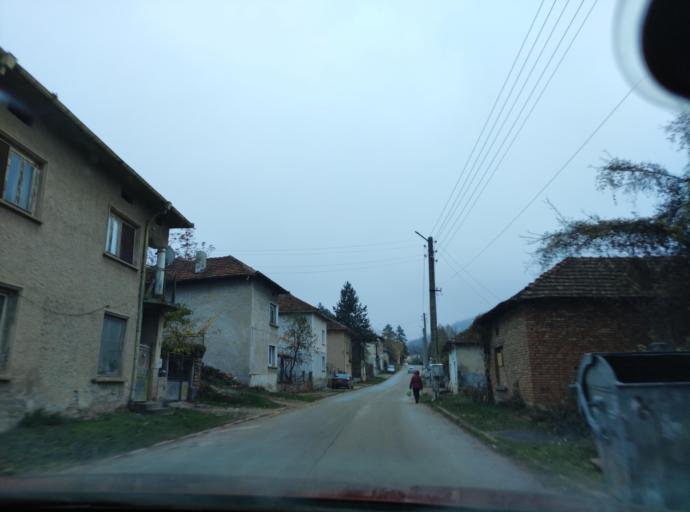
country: BG
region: Lovech
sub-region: Obshtina Yablanitsa
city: Yablanitsa
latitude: 43.1201
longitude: 24.0630
